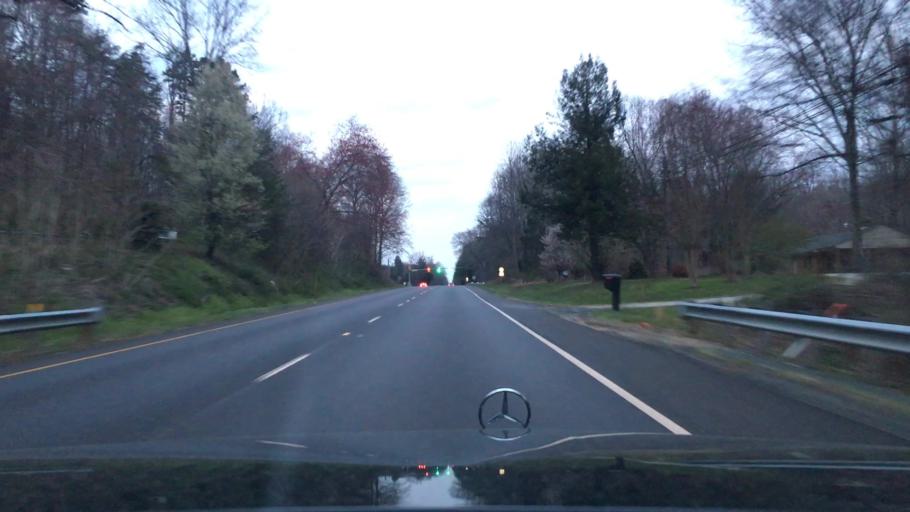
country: US
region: Virginia
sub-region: Albemarle County
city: Hollymead
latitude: 38.1619
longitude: -78.4158
